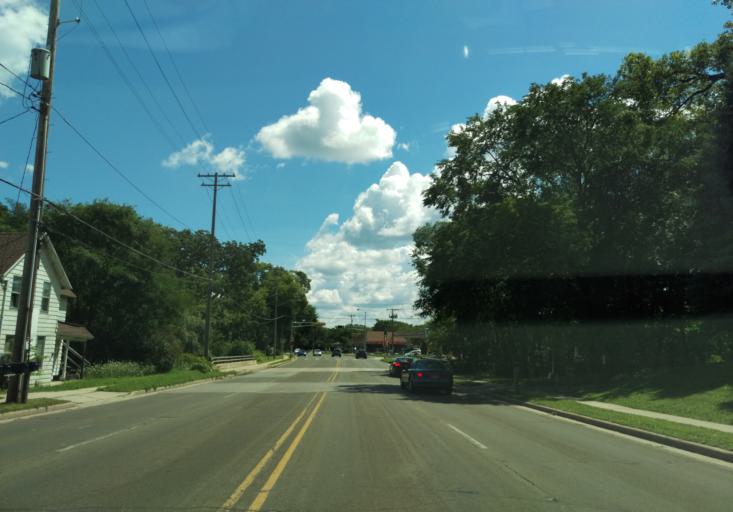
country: US
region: Wisconsin
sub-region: Dane County
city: Middleton
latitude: 43.1046
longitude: -89.4940
